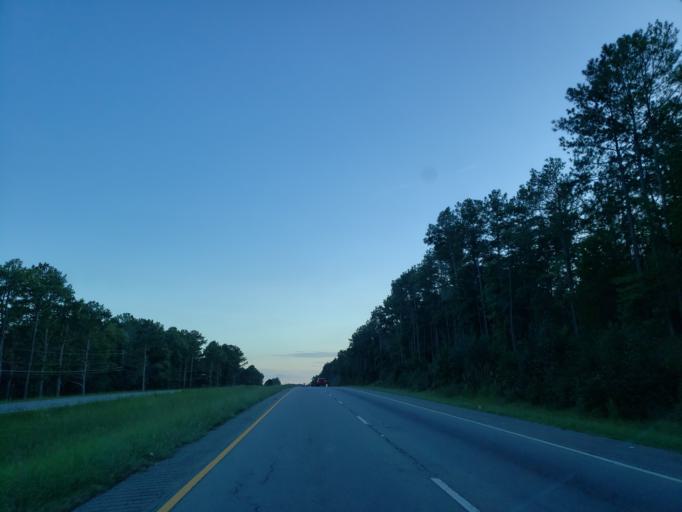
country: US
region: Georgia
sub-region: Floyd County
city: Lindale
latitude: 34.2098
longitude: -85.1905
